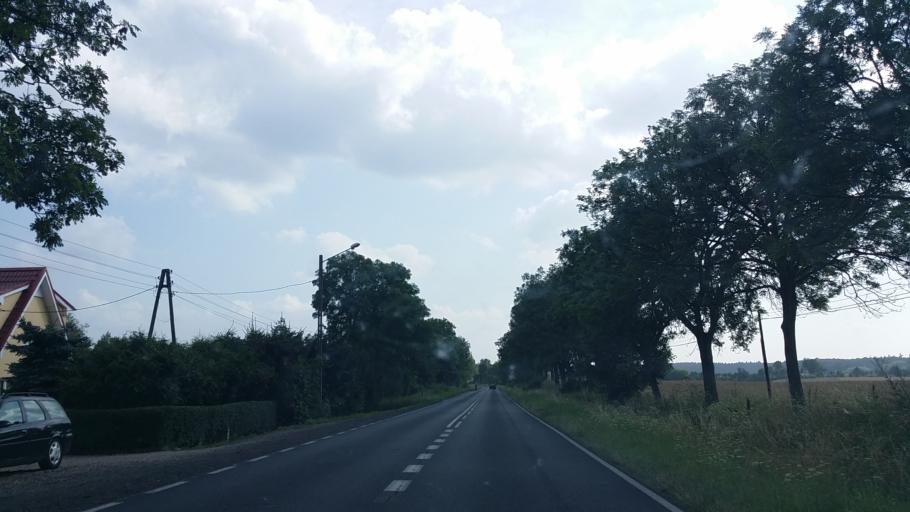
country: PL
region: West Pomeranian Voivodeship
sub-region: Powiat mysliborski
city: Barlinek
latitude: 52.9659
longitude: 15.1851
